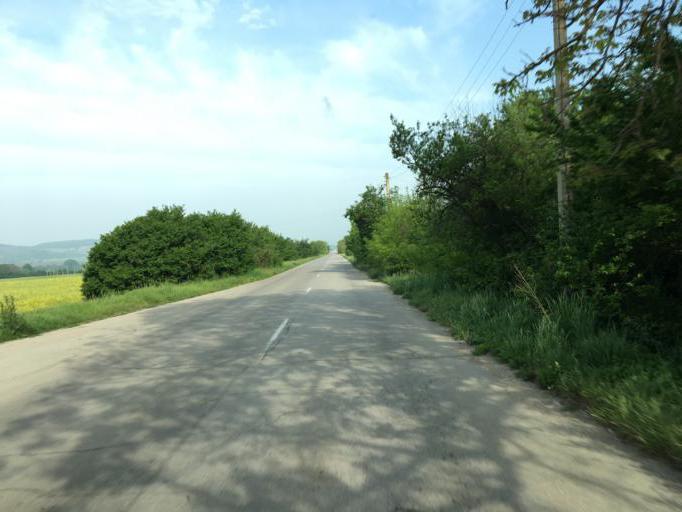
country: BG
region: Kyustendil
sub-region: Obshtina Bobovdol
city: Bobovdol
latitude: 42.4623
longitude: 23.0890
